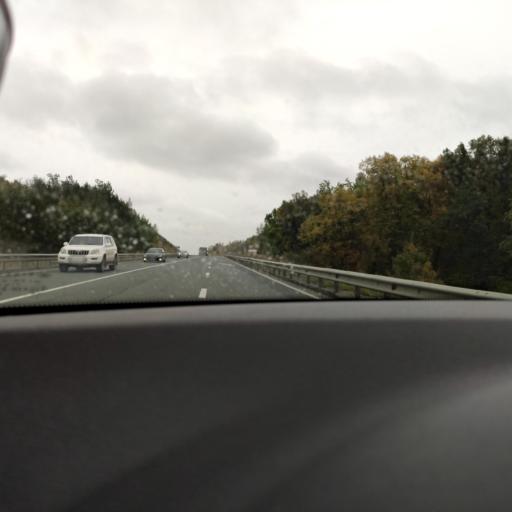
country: RU
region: Samara
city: Mirnyy
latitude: 53.6024
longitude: 50.2757
